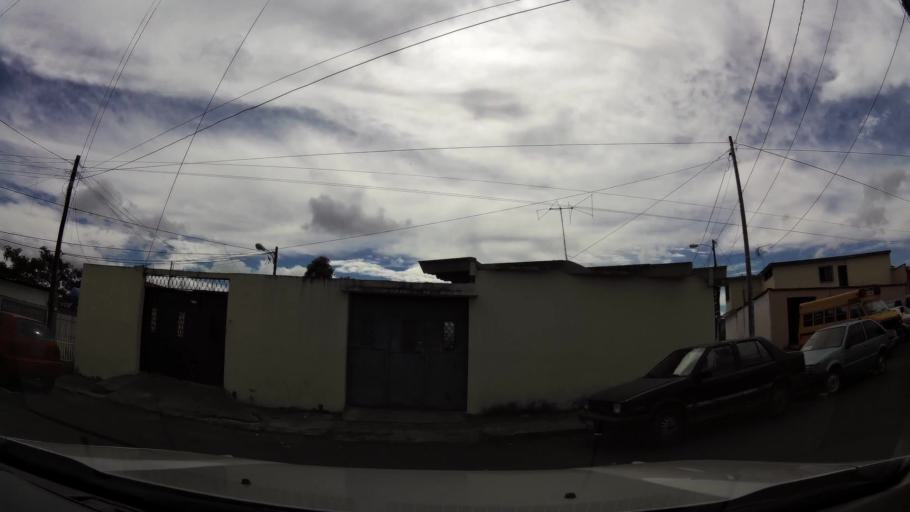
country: GT
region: Guatemala
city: Mixco
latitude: 14.6702
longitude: -90.5646
